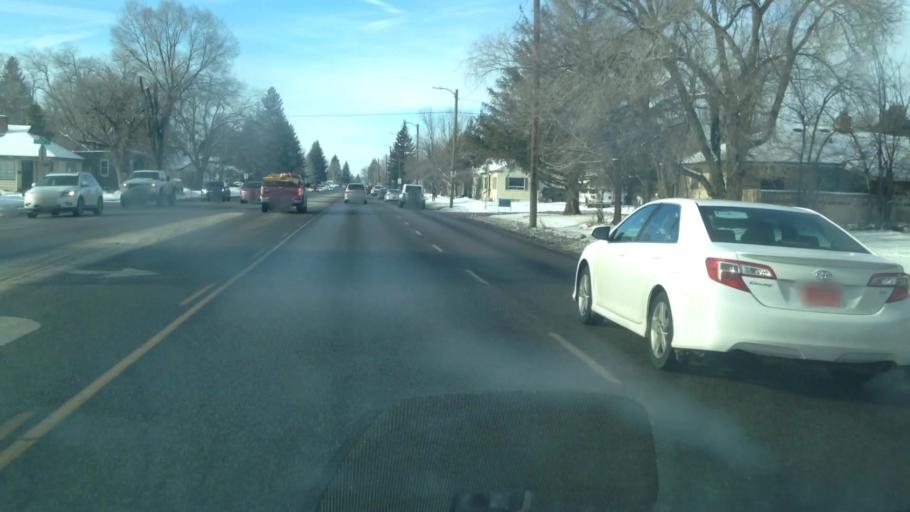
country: US
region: Idaho
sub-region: Bonneville County
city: Idaho Falls
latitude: 43.4826
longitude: -112.0254
